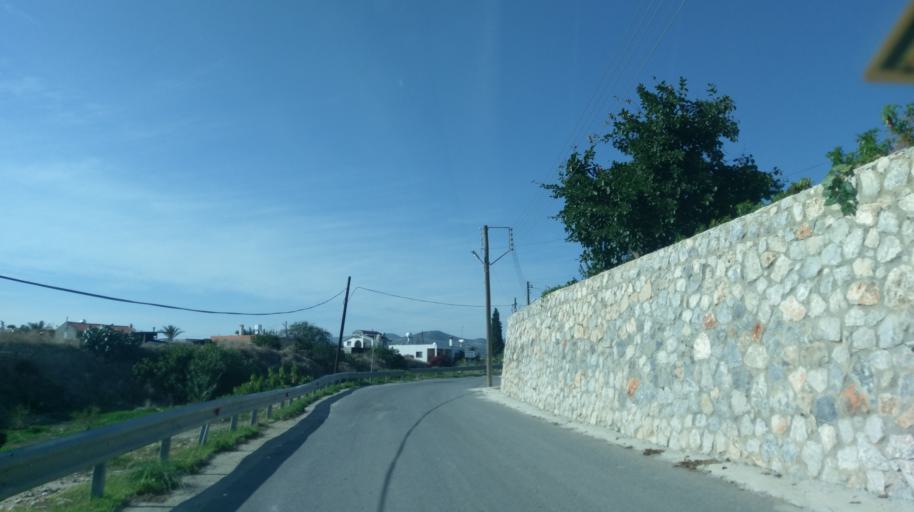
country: CY
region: Ammochostos
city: Trikomo
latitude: 35.3387
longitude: 33.8732
